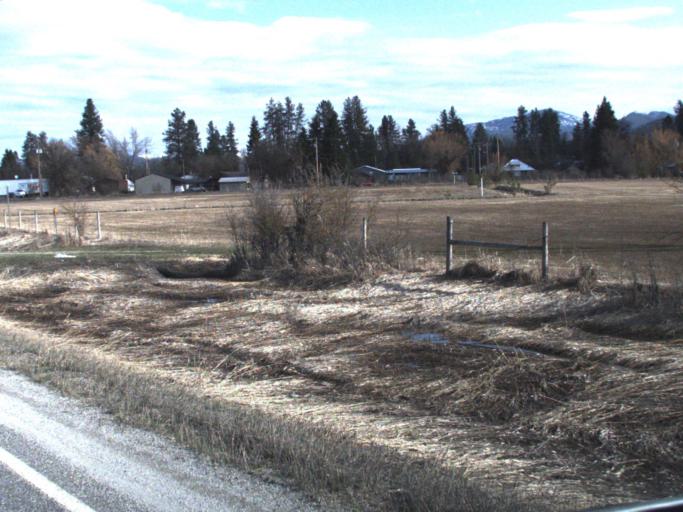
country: US
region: Washington
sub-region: Pend Oreille County
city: Newport
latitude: 48.3342
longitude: -117.3033
